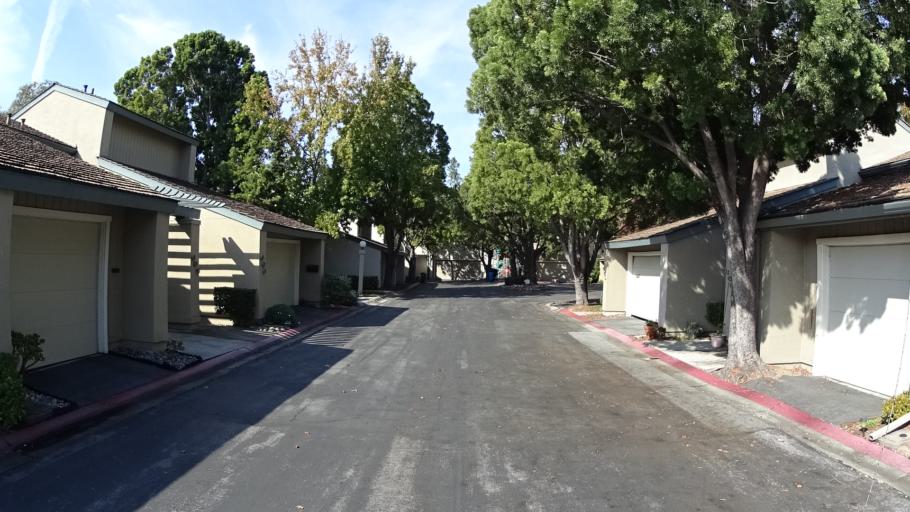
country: US
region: California
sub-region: San Mateo County
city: Foster City
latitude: 37.5502
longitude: -122.2796
